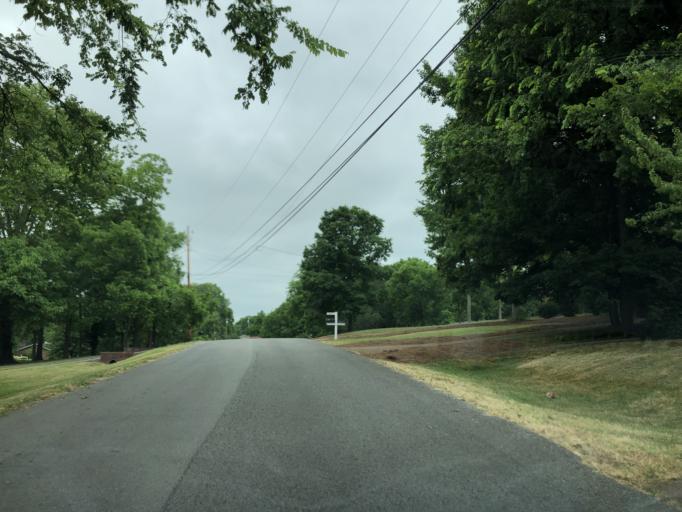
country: US
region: Tennessee
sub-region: Davidson County
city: Goodlettsville
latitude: 36.2814
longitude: -86.7364
